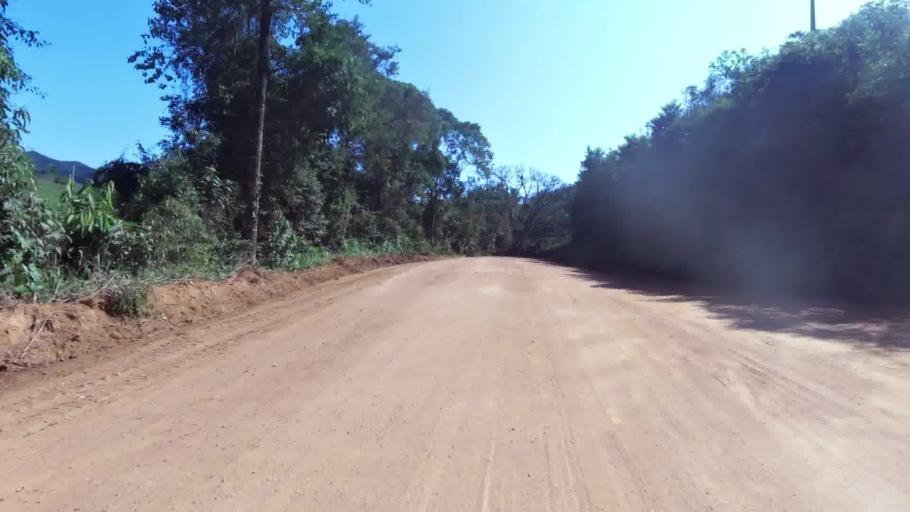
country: BR
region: Espirito Santo
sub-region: Alfredo Chaves
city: Alfredo Chaves
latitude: -20.5365
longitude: -40.8357
